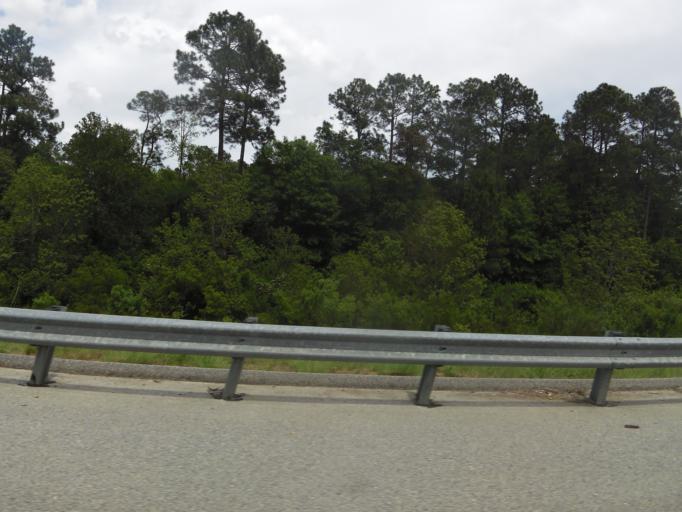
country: US
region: Georgia
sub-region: Emanuel County
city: Swainsboro
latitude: 32.5883
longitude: -82.3673
